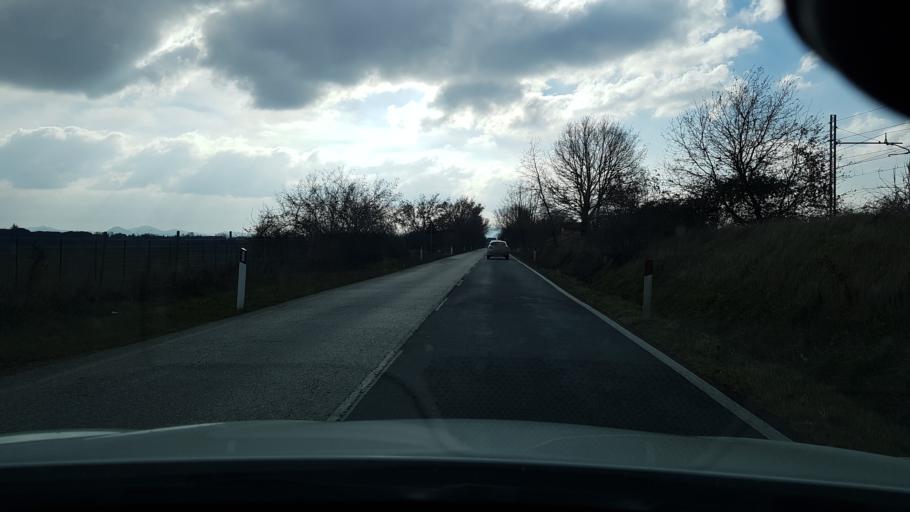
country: IT
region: Umbria
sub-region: Provincia di Perugia
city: Castiglione del Lago
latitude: 43.1399
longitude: 12.0252
